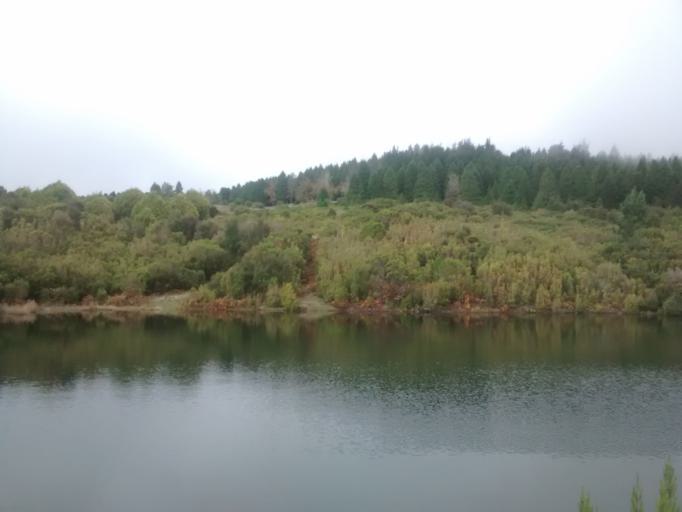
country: PT
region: Madeira
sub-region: Santa Cruz
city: Camacha
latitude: 32.7182
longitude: -16.8654
